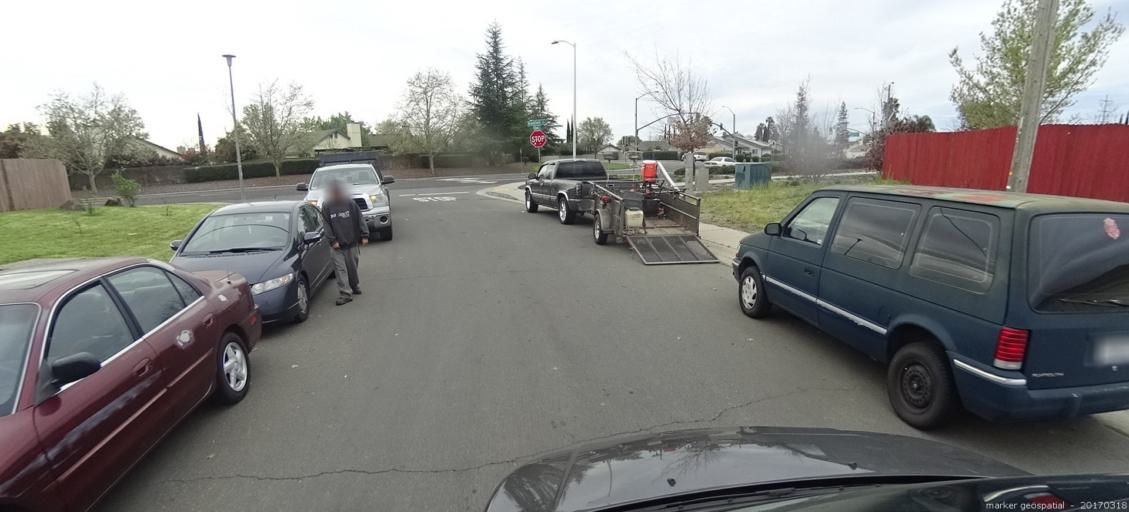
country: US
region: California
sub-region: Sacramento County
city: Parkway
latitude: 38.4817
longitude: -121.4626
